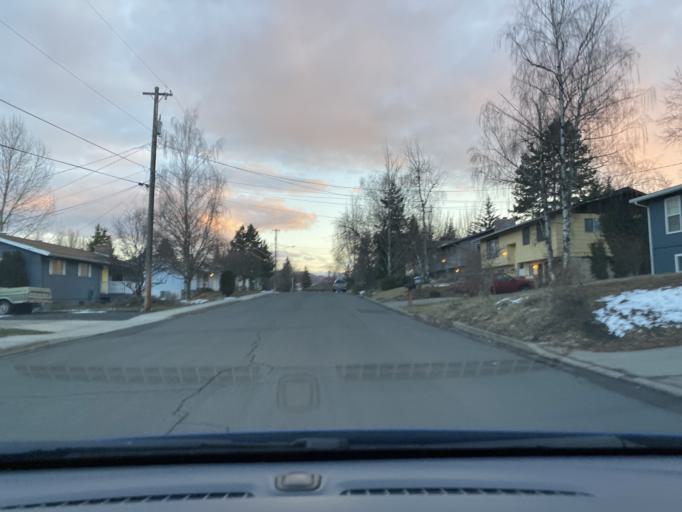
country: US
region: Idaho
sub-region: Latah County
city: Moscow
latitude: 46.7422
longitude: -116.9831
